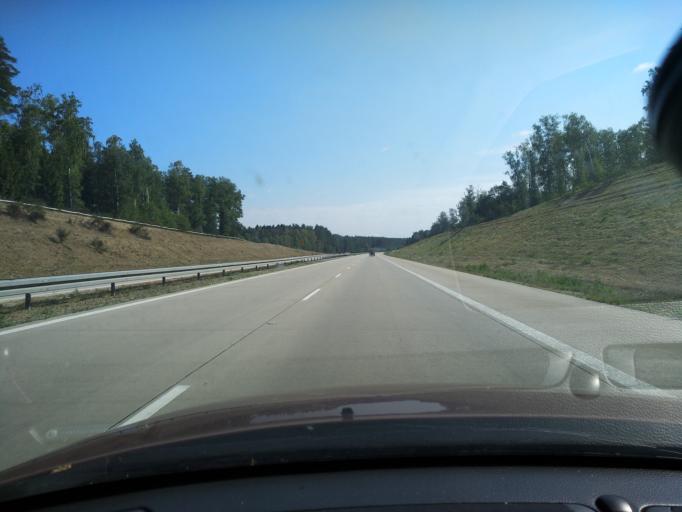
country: PL
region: Lower Silesian Voivodeship
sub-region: Powiat lubanski
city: Pisarzowice
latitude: 51.2146
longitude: 15.2062
